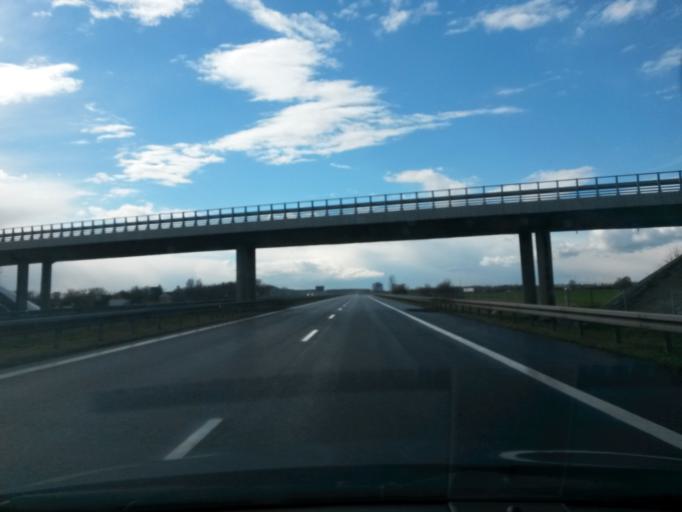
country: PL
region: Greater Poland Voivodeship
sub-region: Powiat slupecki
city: Strzalkowo
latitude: 52.2588
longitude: 17.7951
